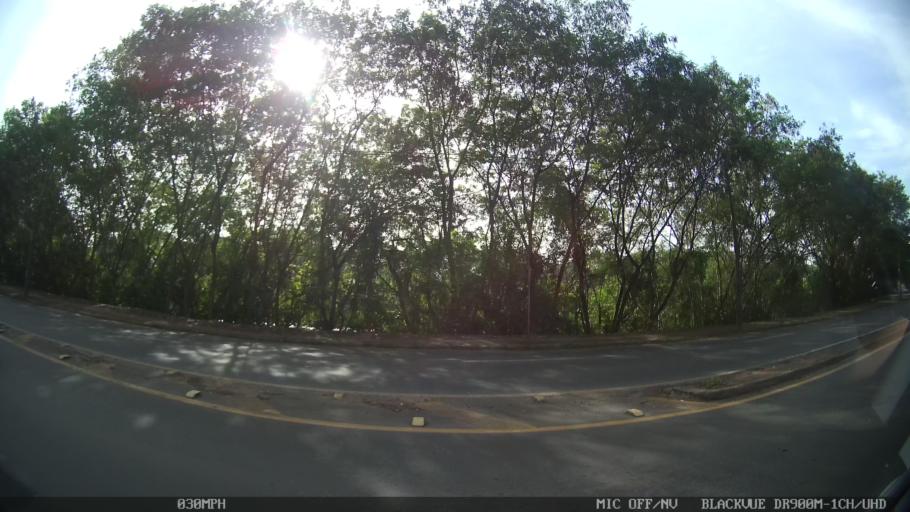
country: BR
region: Sao Paulo
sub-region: Piracicaba
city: Piracicaba
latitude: -22.7178
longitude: -47.6773
